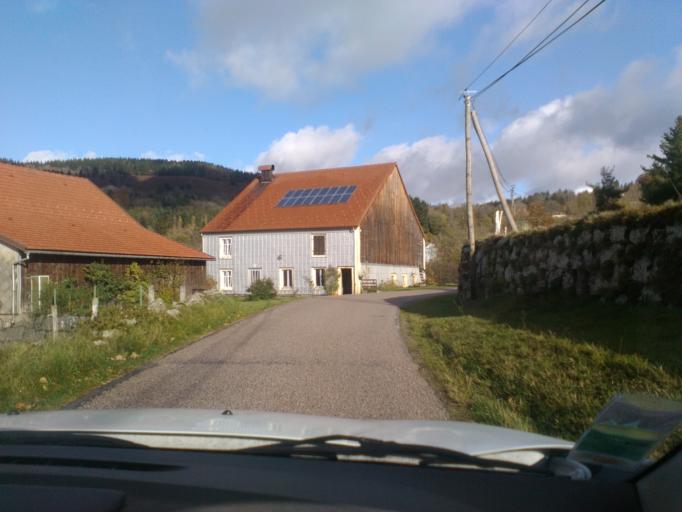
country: FR
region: Lorraine
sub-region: Departement des Vosges
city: Saulxures-sur-Moselotte
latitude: 47.9682
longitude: 6.7912
